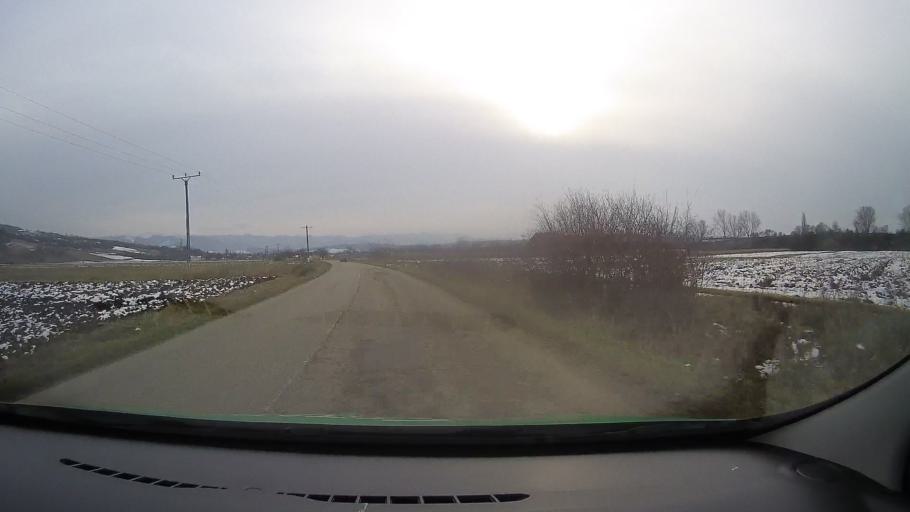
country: RO
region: Hunedoara
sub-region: Comuna Romos
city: Romos
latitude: 45.8590
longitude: 23.2716
